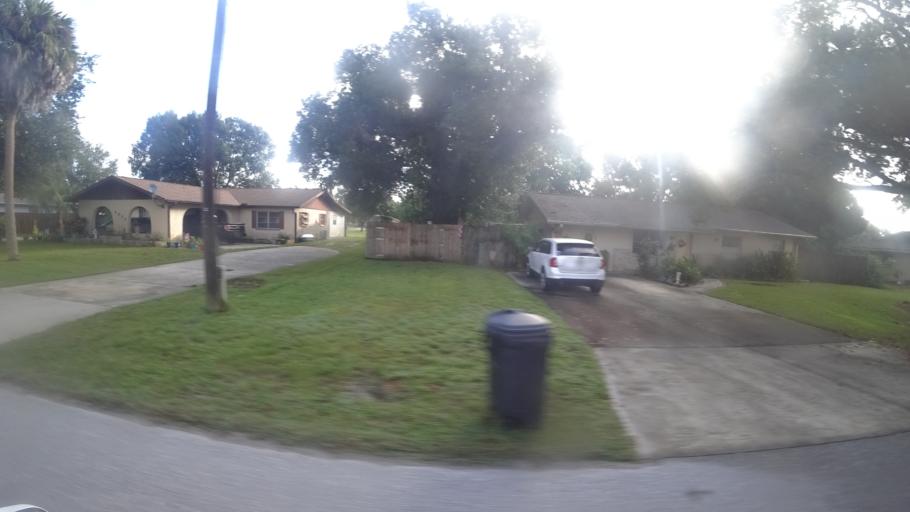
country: US
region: Florida
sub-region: Manatee County
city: Ellenton
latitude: 27.5382
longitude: -82.4827
